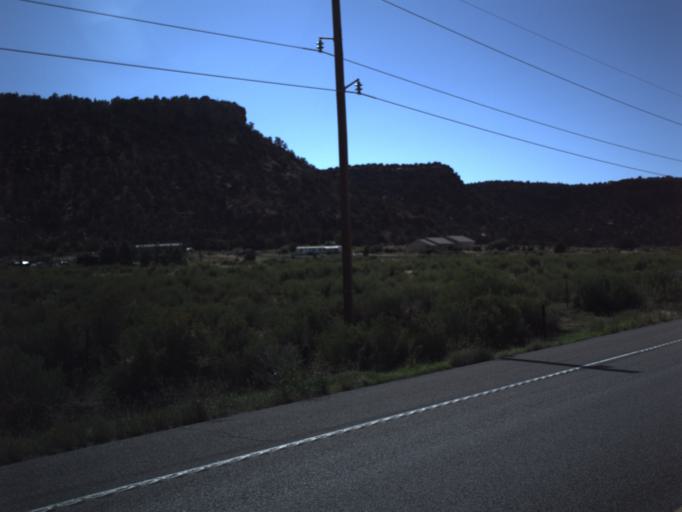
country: US
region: Utah
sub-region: Washington County
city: LaVerkin
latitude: 37.1079
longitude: -113.1419
